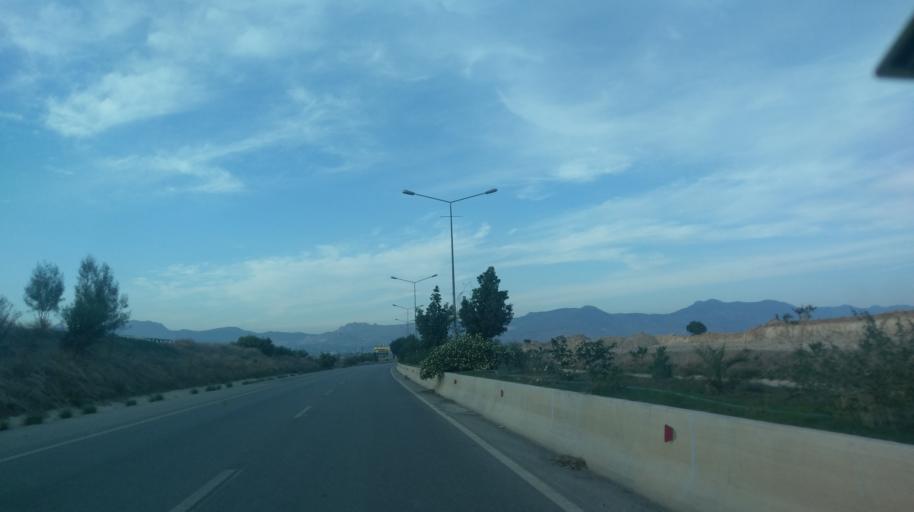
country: CY
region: Lefkosia
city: Geri
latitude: 35.1749
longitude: 33.5024
